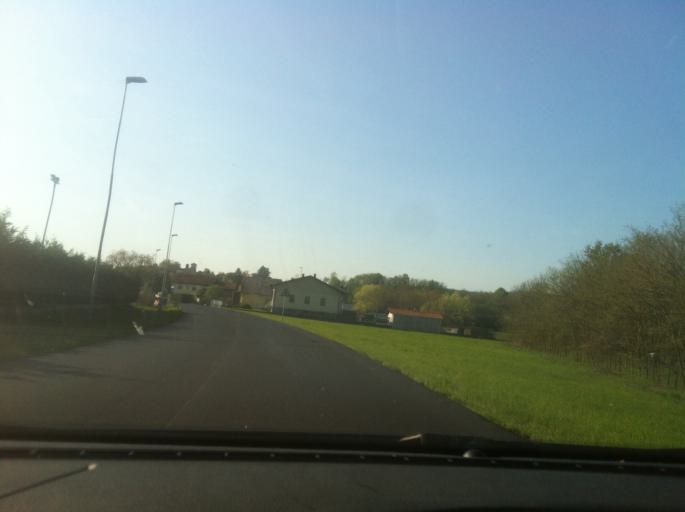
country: IT
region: Piedmont
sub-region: Provincia di Torino
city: Mercenasco
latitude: 45.3654
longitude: 7.8764
